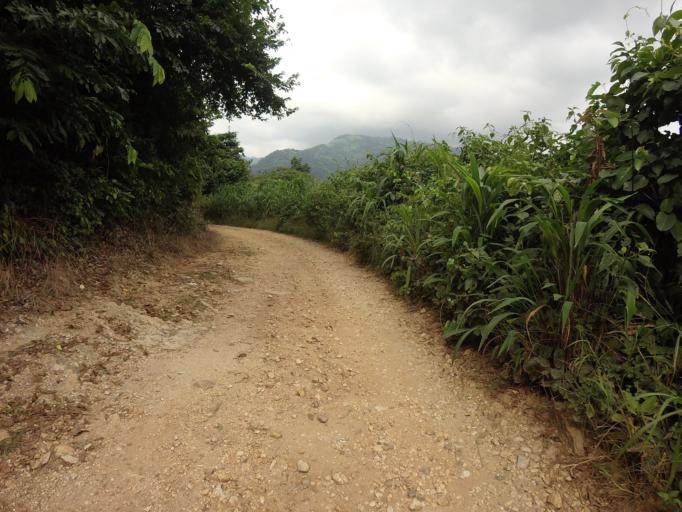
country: TG
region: Plateaux
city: Kpalime
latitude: 6.8652
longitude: 0.4404
